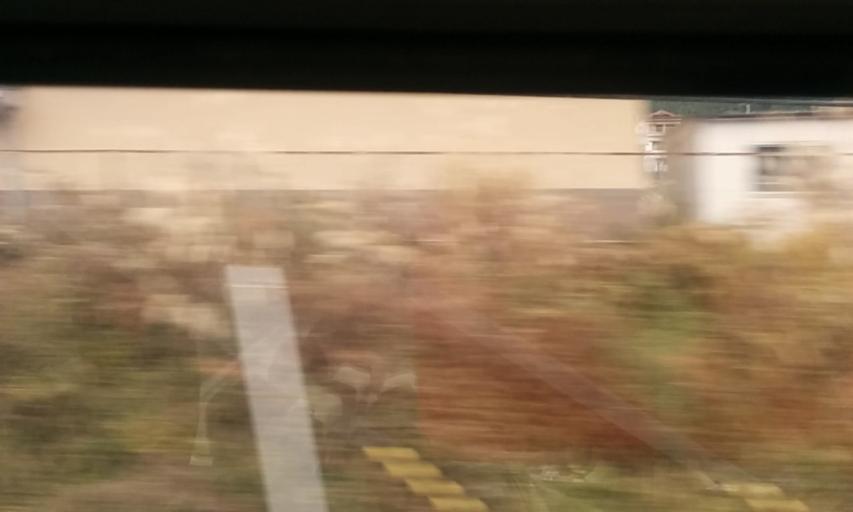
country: JP
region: Gifu
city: Nakatsugawa
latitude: 35.6073
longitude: 137.6095
